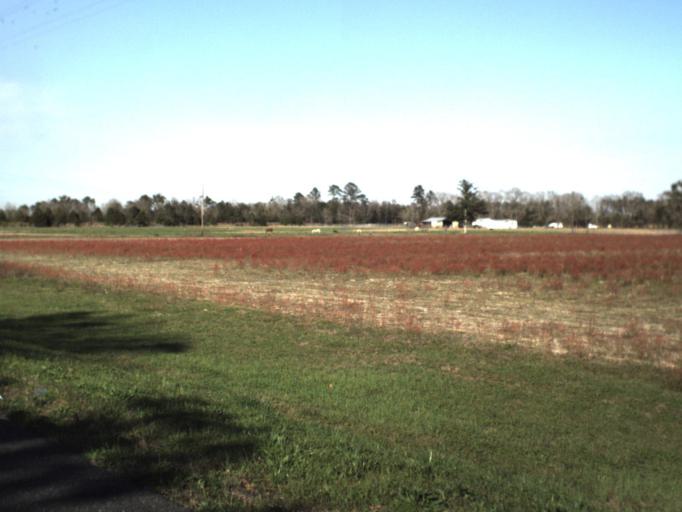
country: US
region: Florida
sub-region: Calhoun County
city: Blountstown
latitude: 30.4865
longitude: -85.2002
